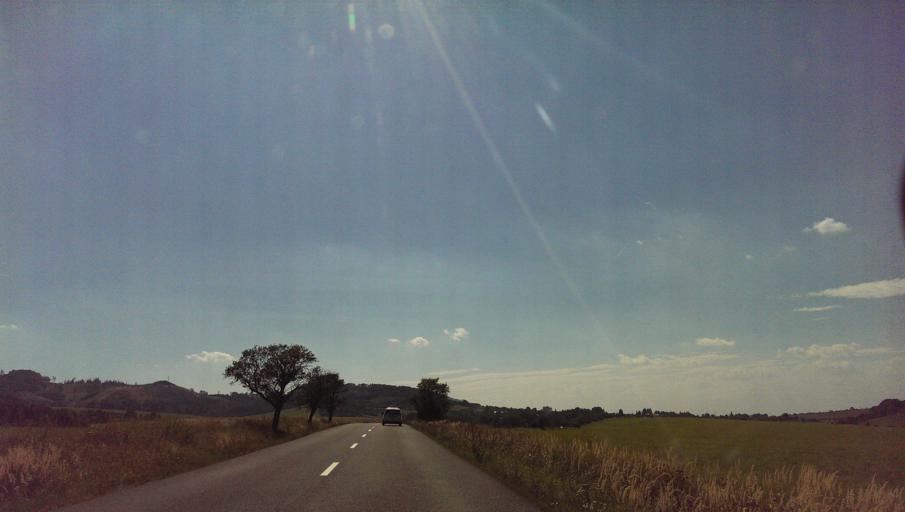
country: CZ
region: Zlin
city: Kelc
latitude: 49.4458
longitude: 17.8594
